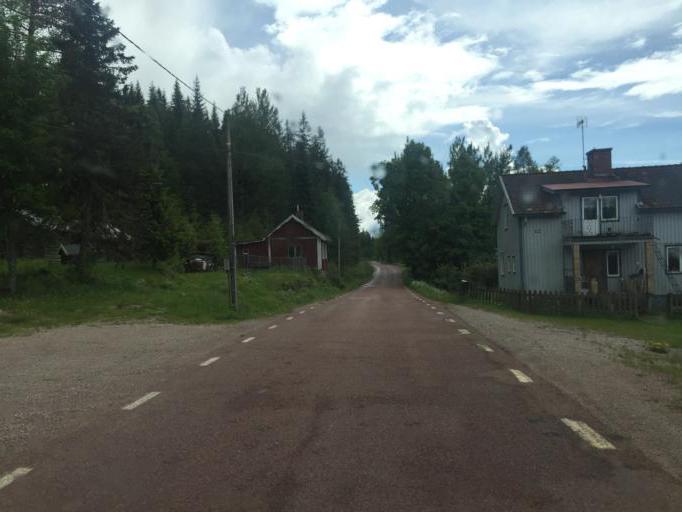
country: SE
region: Dalarna
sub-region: Malung-Saelens kommun
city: Malung
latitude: 60.3764
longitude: 13.8710
